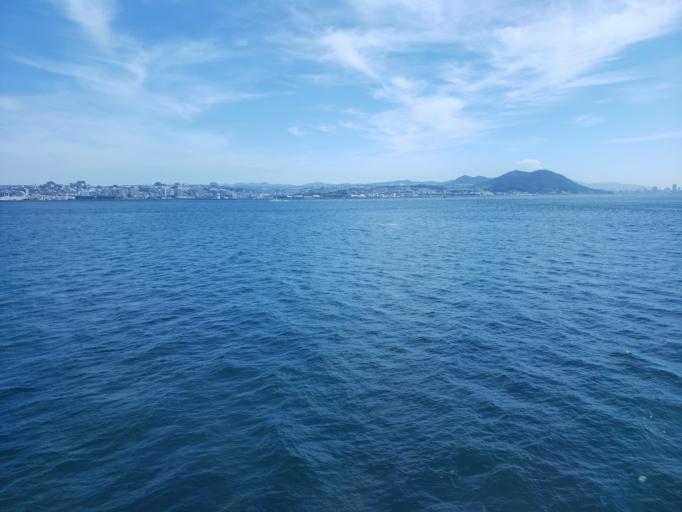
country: JP
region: Hyogo
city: Akashi
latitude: 34.6047
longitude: 135.0503
